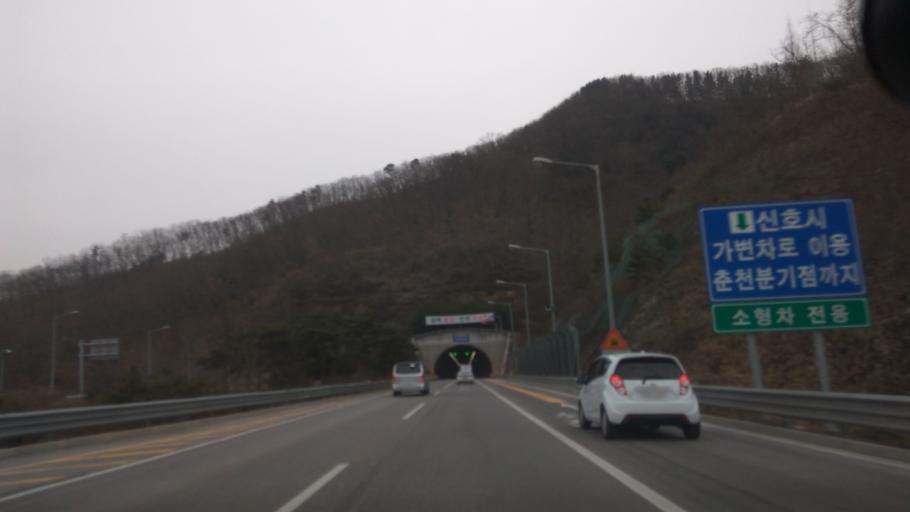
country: KR
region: Gyeonggi-do
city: Gapyeong
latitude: 37.7193
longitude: 127.5721
